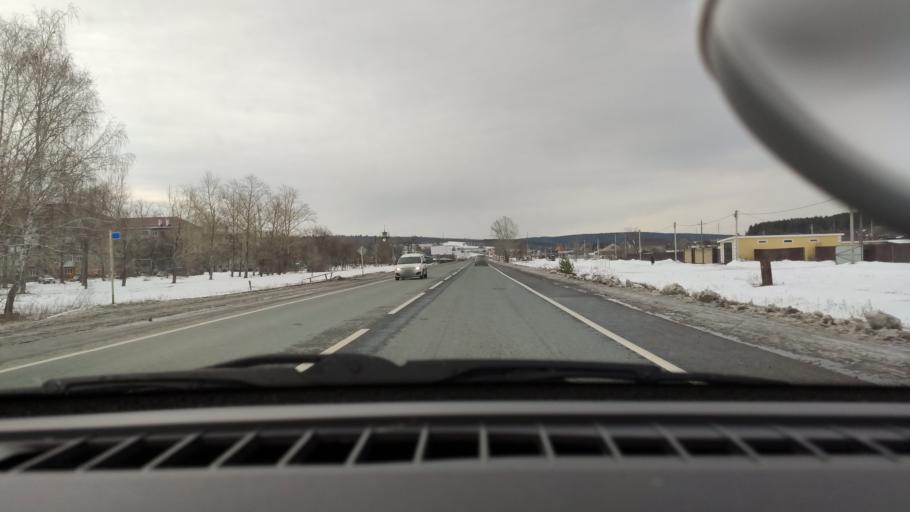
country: RU
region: Samara
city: Kurumoch
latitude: 53.4851
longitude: 50.0219
